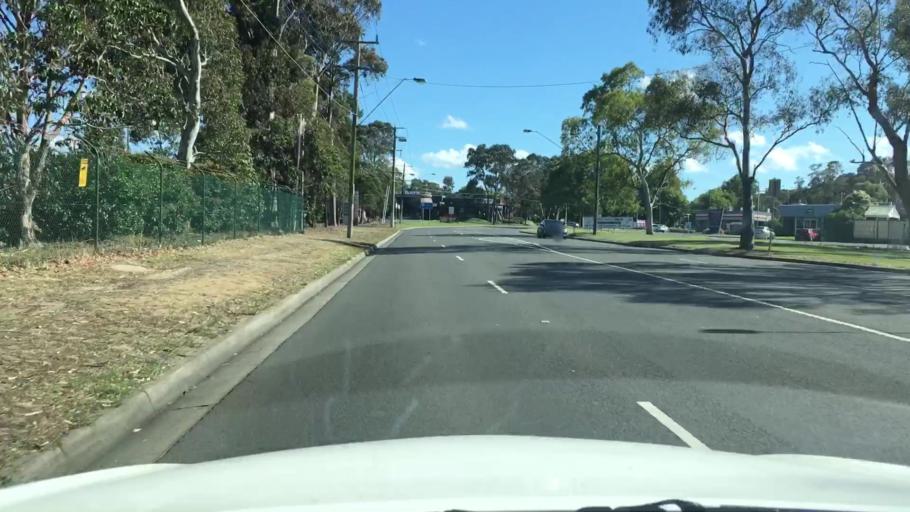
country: AU
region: Victoria
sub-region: Greater Dandenong
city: Noble Park
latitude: -37.9496
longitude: 145.1713
